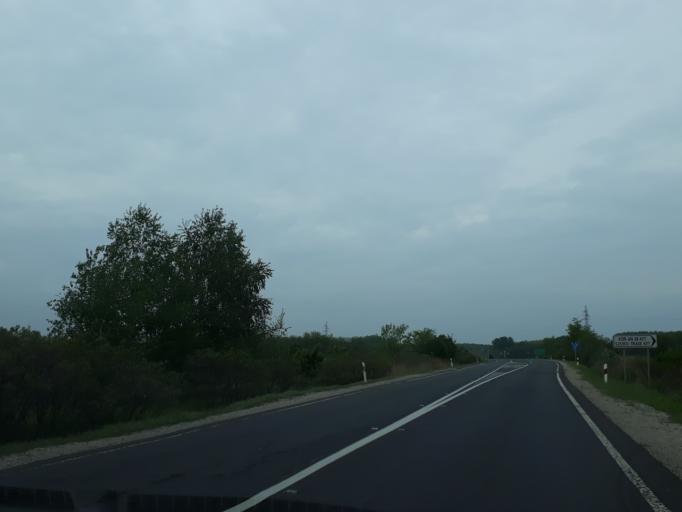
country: HU
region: Szabolcs-Szatmar-Bereg
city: Demecser
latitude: 48.0674
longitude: 21.9376
